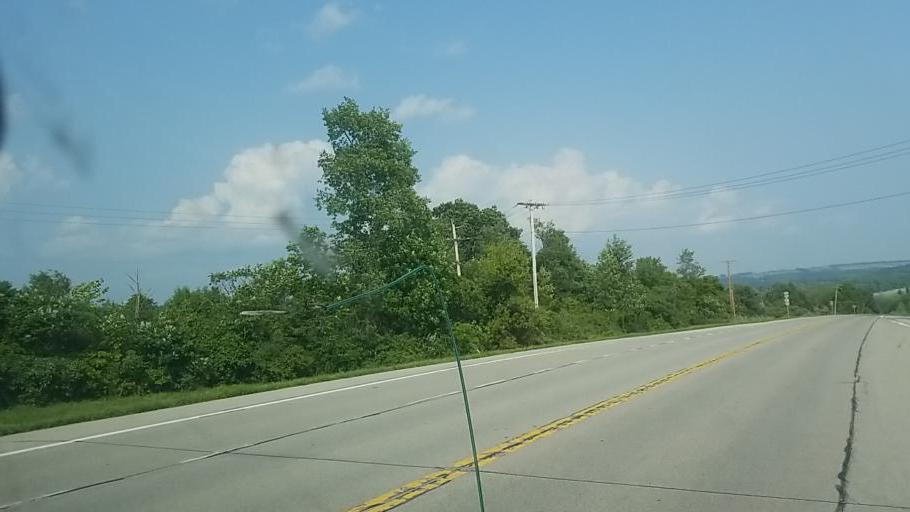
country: US
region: New York
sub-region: Montgomery County
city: Fonda
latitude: 42.9353
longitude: -74.3331
